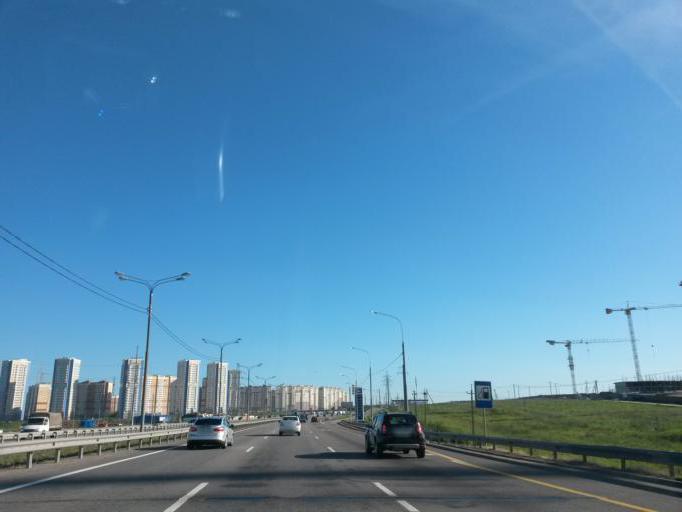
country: RU
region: Moskovskaya
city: Vostryakovo
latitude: 55.3870
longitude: 37.7762
